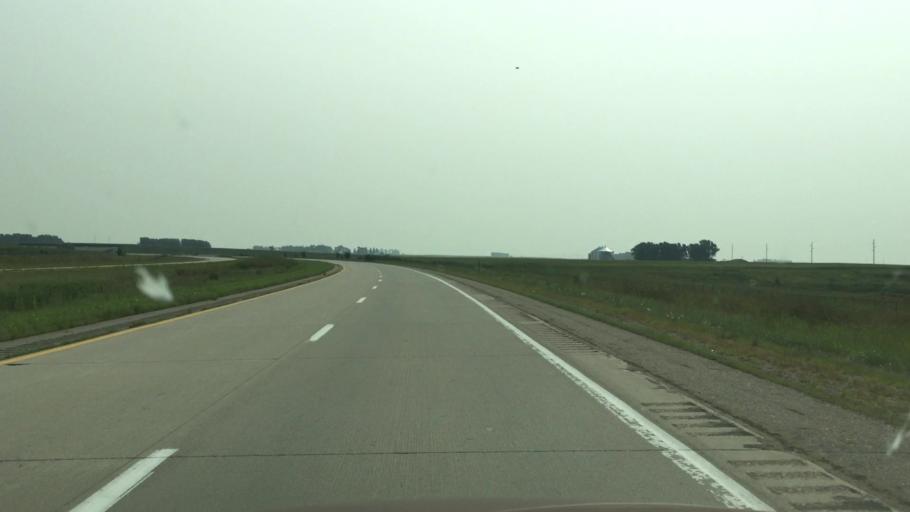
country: US
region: Iowa
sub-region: Osceola County
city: Sibley
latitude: 43.3842
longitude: -95.7325
